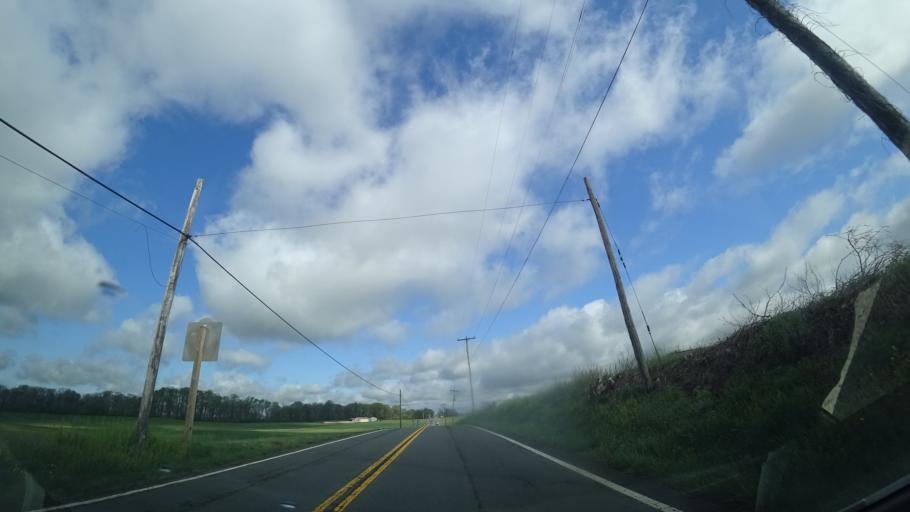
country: US
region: Maryland
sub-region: Montgomery County
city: Poolesville
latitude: 39.2253
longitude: -77.4267
